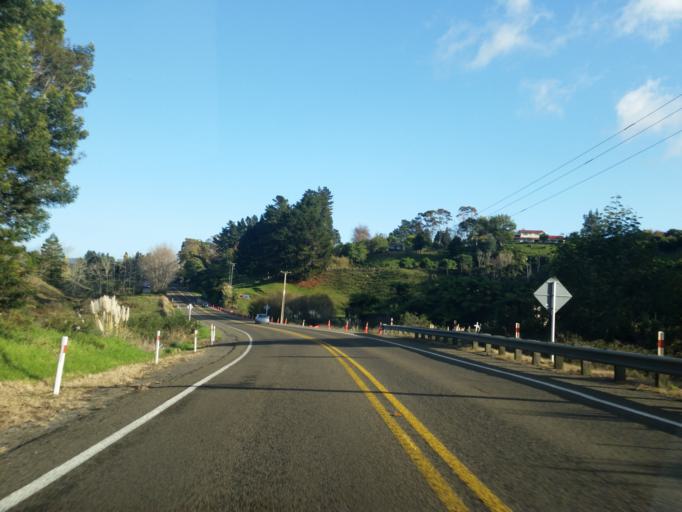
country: NZ
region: Bay of Plenty
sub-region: Tauranga City
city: Tauranga
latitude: -37.6840
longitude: 176.0349
